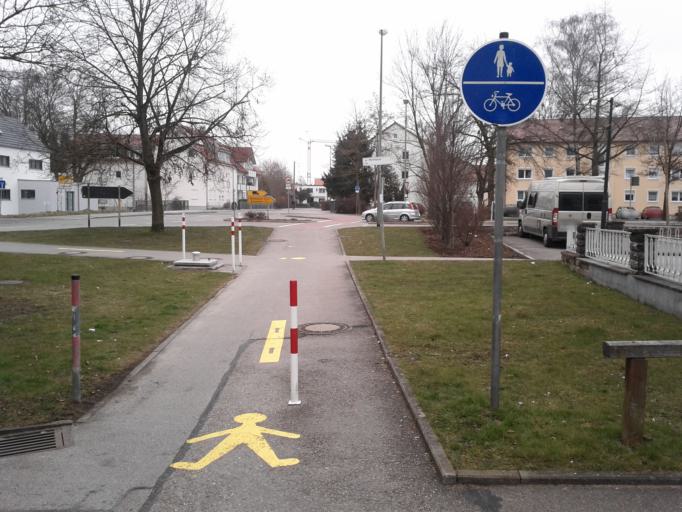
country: DE
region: Bavaria
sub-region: Swabia
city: Guenzburg
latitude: 48.4517
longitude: 10.2674
